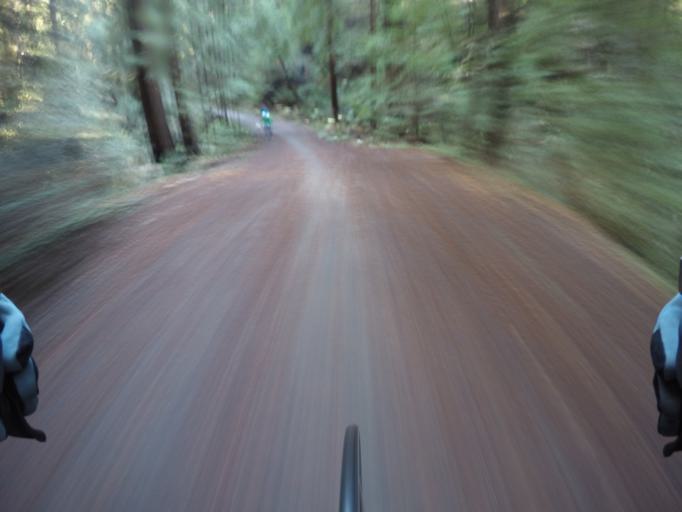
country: US
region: California
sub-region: Santa Cruz County
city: Pasatiempo
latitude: 37.0148
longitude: -122.0383
